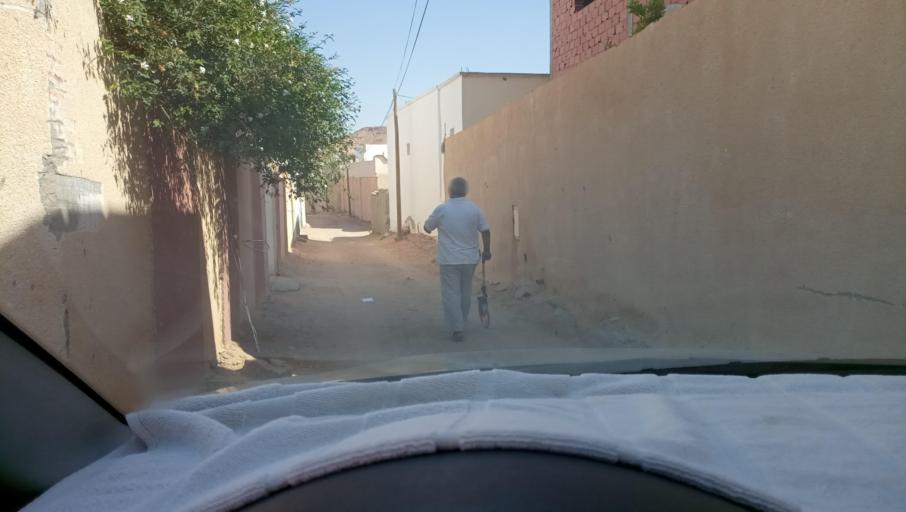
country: TN
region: Tataouine
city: Tataouine
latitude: 32.9780
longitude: 10.3854
